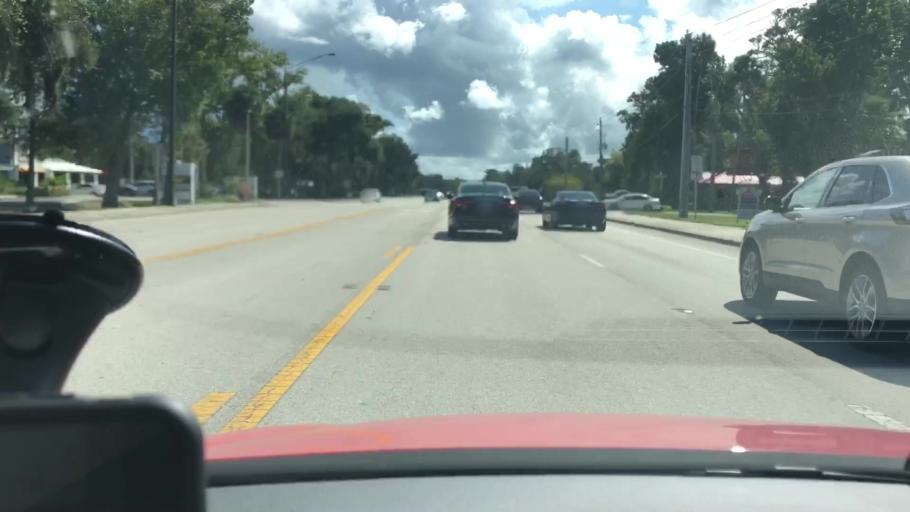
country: US
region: Florida
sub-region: Volusia County
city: Port Orange
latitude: 29.1305
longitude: -81.0068
